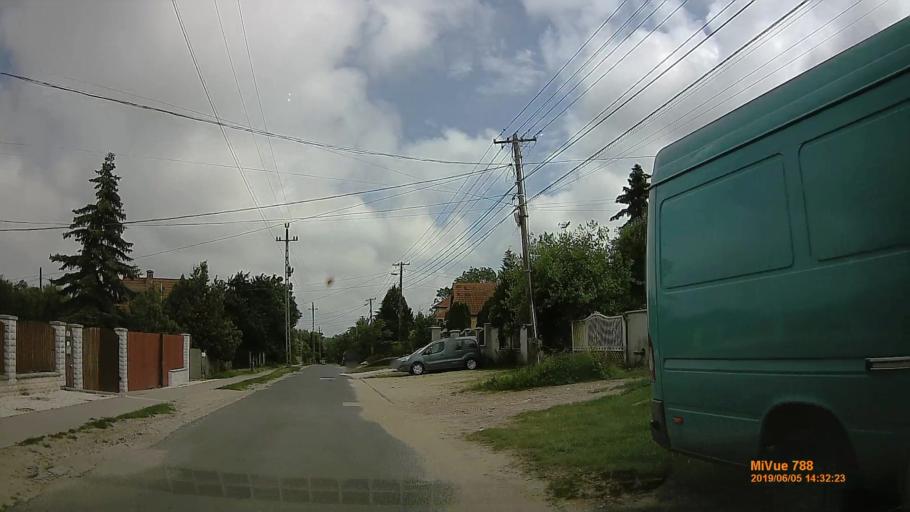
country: HU
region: Pest
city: Kistarcsa
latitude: 47.5561
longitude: 19.2687
